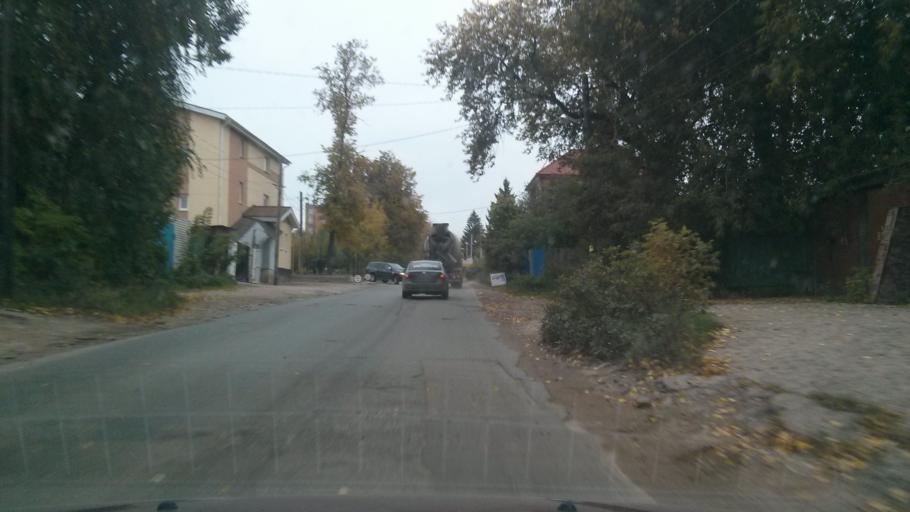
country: RU
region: Nizjnij Novgorod
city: Nizhniy Novgorod
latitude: 56.3039
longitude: 44.0260
